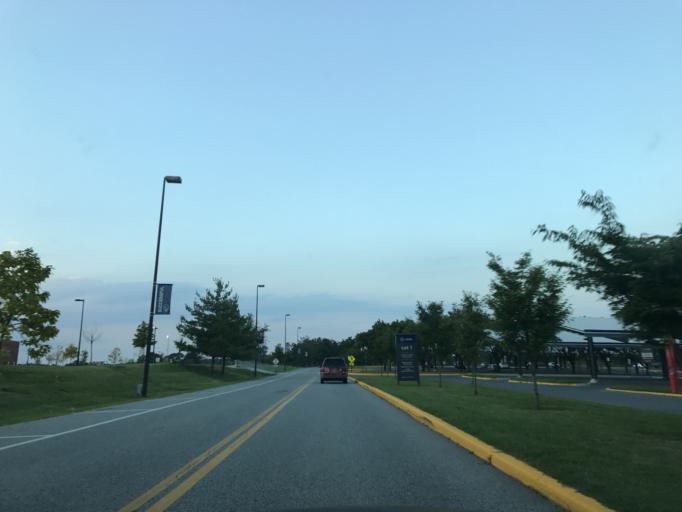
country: US
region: Maryland
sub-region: Baltimore County
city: Dundalk
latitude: 39.2656
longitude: -76.5150
